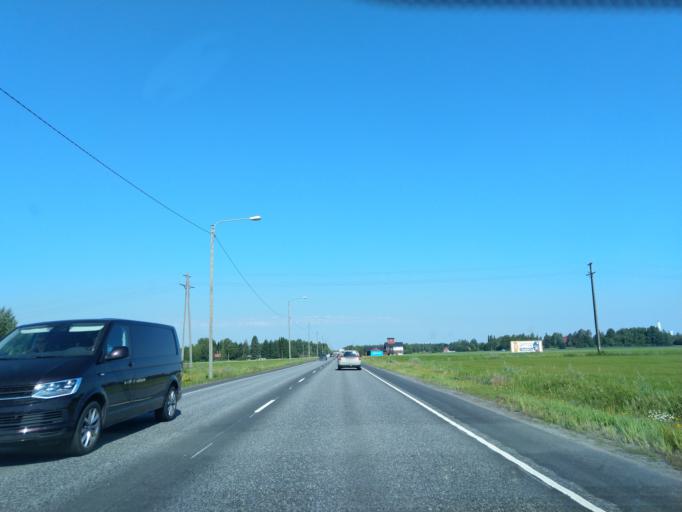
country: FI
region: Satakunta
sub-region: Pori
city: Nakkila
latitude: 61.3543
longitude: 22.0074
